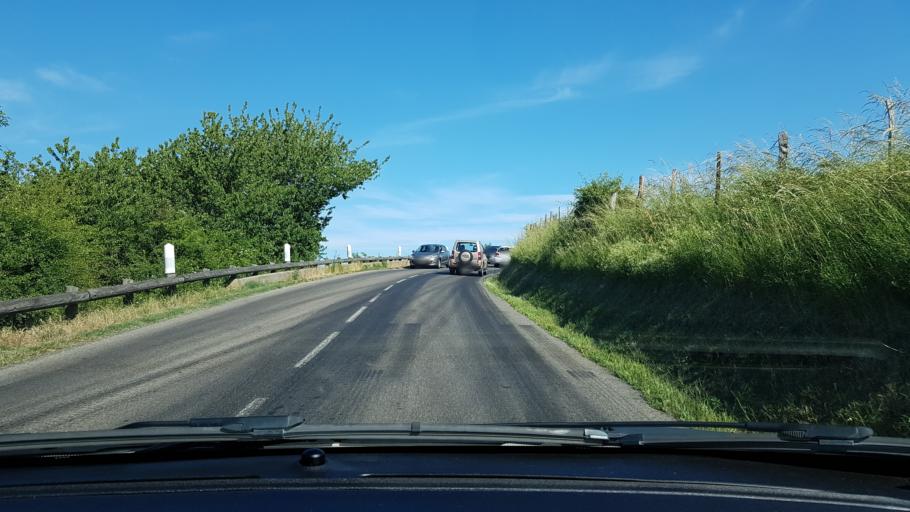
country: FR
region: Rhone-Alpes
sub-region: Departement du Rhone
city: Saint-Didier-sous-Riverie
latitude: 45.5981
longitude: 4.5982
